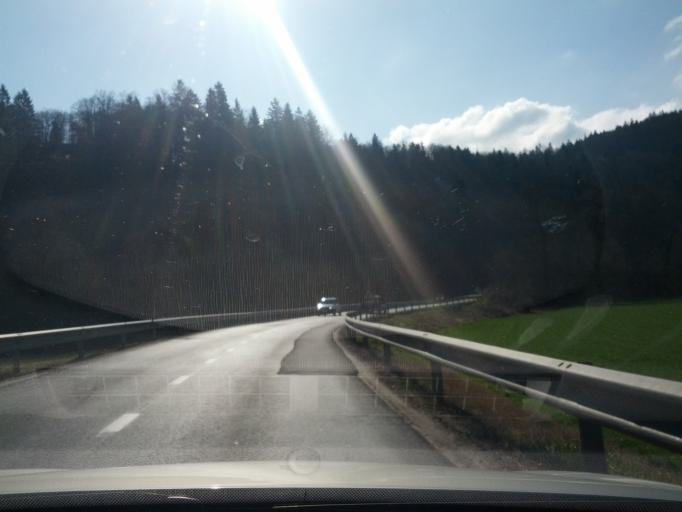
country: SI
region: Litija
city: Litija
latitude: 46.0880
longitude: 14.8367
